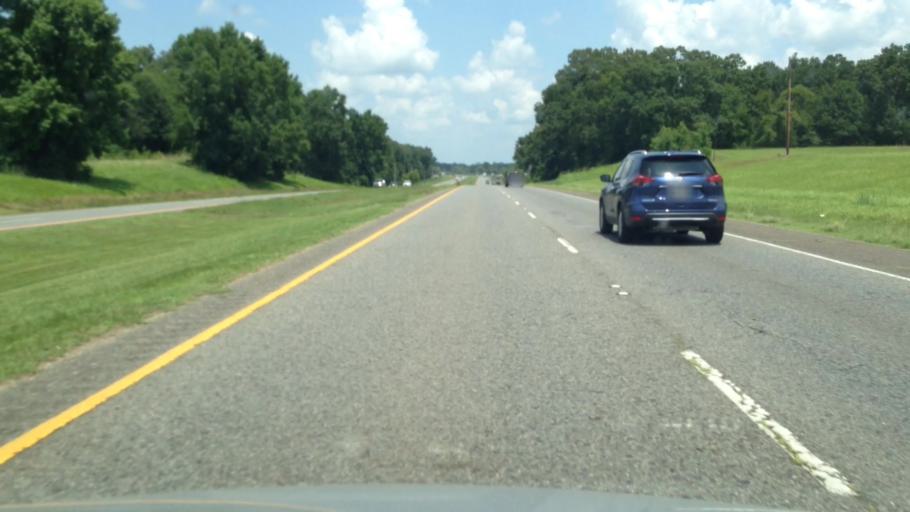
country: US
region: Louisiana
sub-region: Saint Landry Parish
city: Opelousas
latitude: 30.5388
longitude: -92.0433
